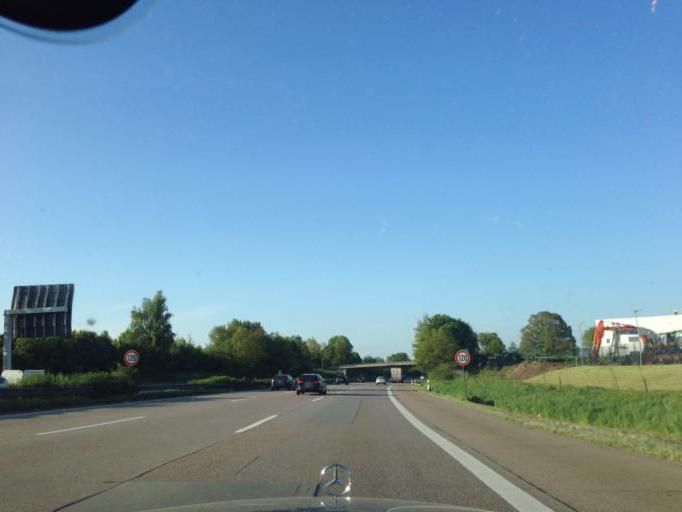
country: DE
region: Schleswig-Holstein
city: Braak
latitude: 53.6185
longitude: 10.2347
